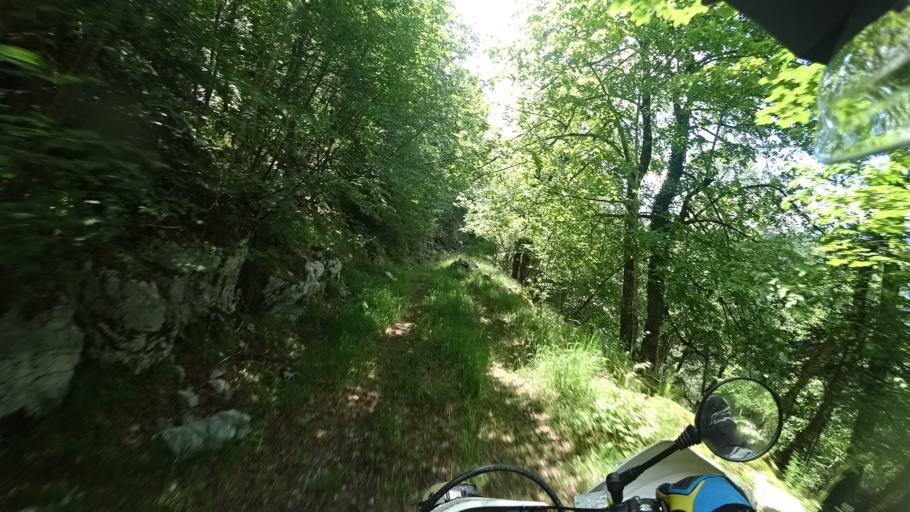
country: SI
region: Osilnica
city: Osilnica
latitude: 45.5006
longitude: 14.7109
